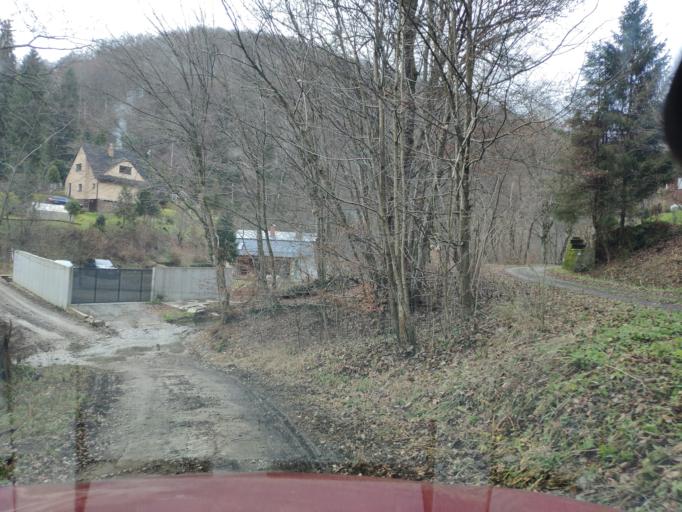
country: SK
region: Kosicky
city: Gelnica
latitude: 48.8176
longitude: 21.0562
